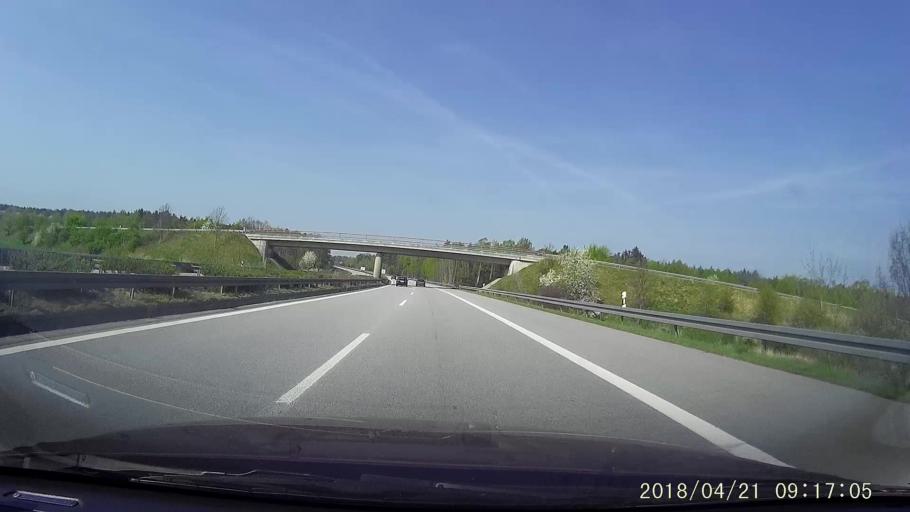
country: DE
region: Saxony
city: Weissenberg
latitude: 51.2138
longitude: 14.7177
